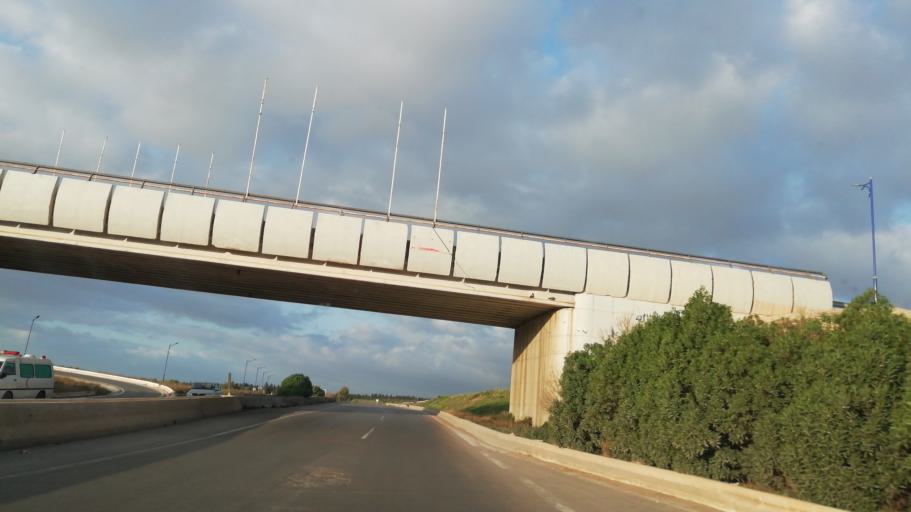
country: DZ
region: Oran
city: Mers el Kebir
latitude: 35.6078
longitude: -0.7501
